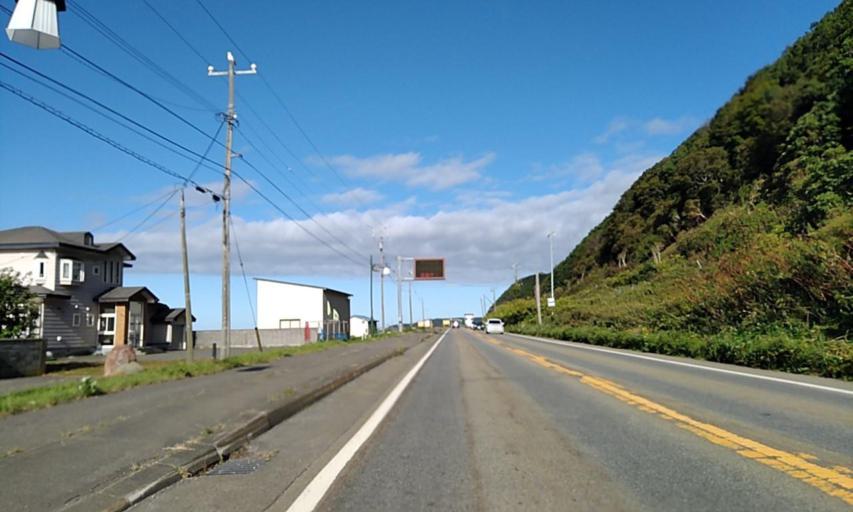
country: JP
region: Hokkaido
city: Shizunai-furukawacho
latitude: 42.2557
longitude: 142.5343
